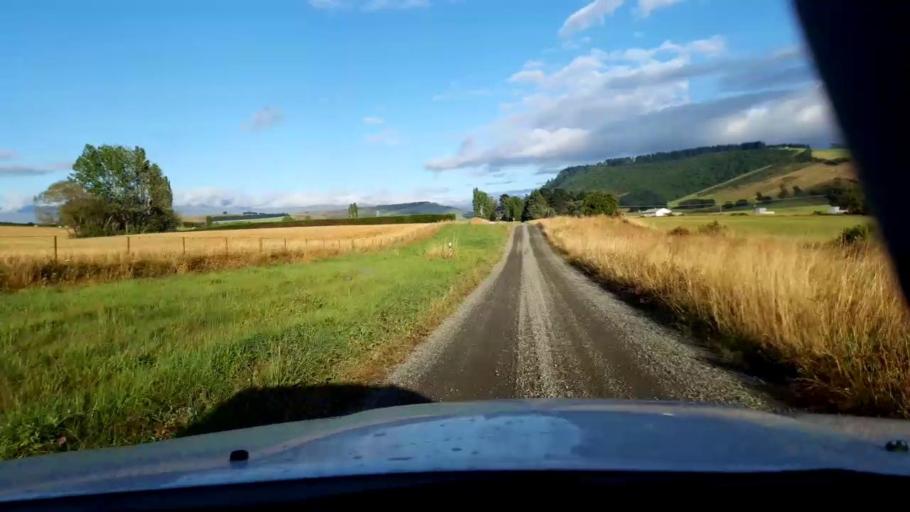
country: NZ
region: Canterbury
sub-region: Timaru District
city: Timaru
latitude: -44.4245
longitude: 171.1100
